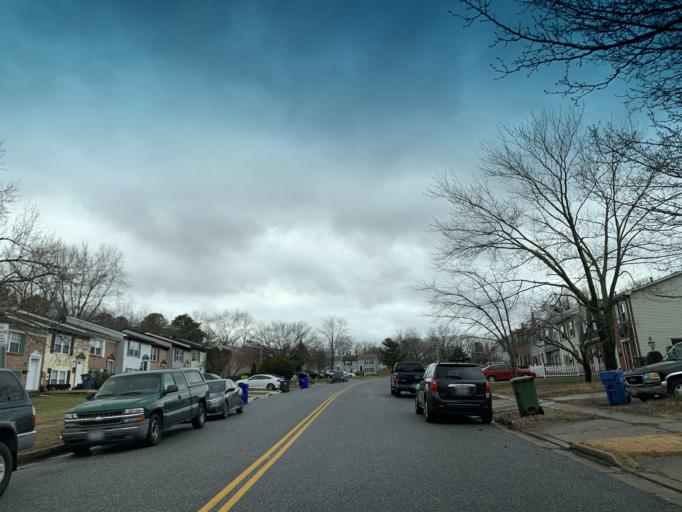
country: US
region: Maryland
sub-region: Harford County
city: Edgewood
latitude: 39.4297
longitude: -76.3174
